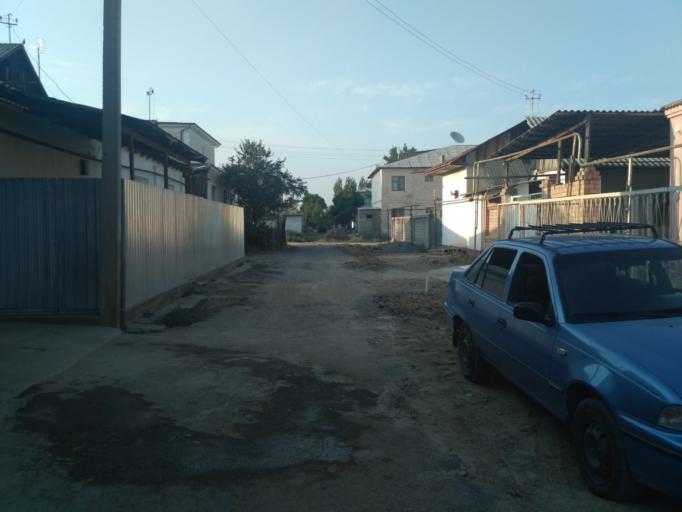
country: UZ
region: Sirdaryo
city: Guliston
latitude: 40.4788
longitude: 68.7795
